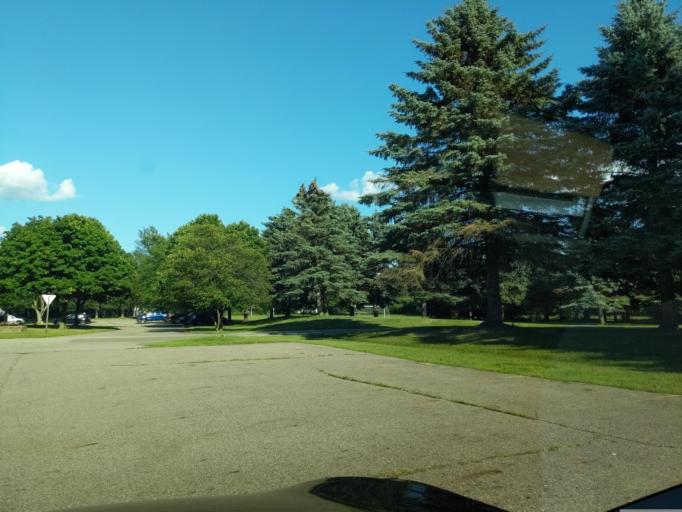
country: US
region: Michigan
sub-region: Ingham County
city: Mason
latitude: 42.5703
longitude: -84.4455
